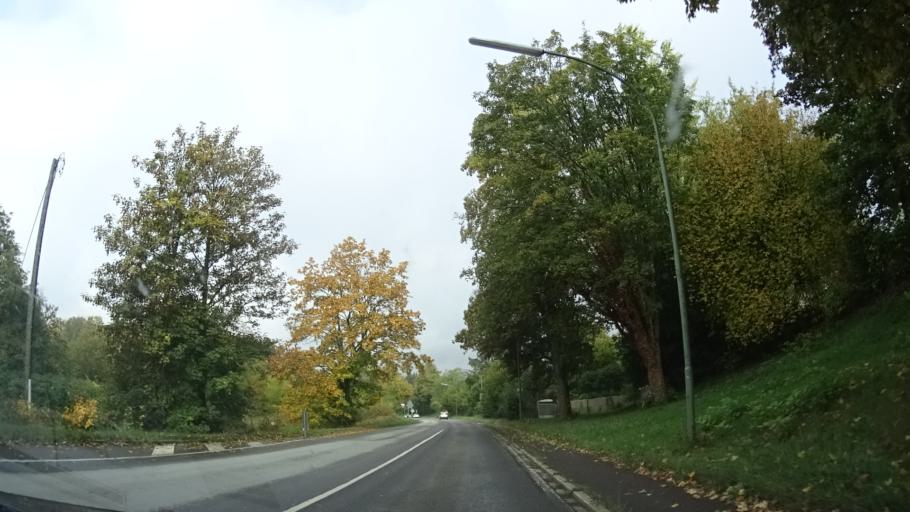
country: DE
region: Baden-Wuerttemberg
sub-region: Karlsruhe Region
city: Pforzheim
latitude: 48.9000
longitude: 8.6909
